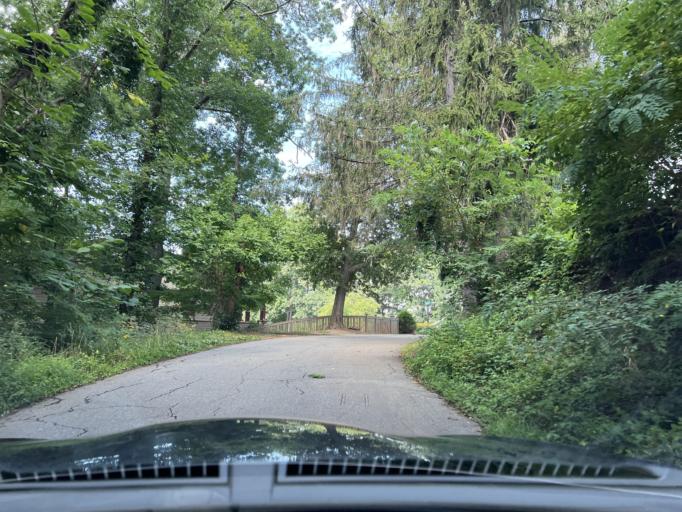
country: US
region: North Carolina
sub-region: Buncombe County
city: Asheville
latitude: 35.5715
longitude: -82.5410
